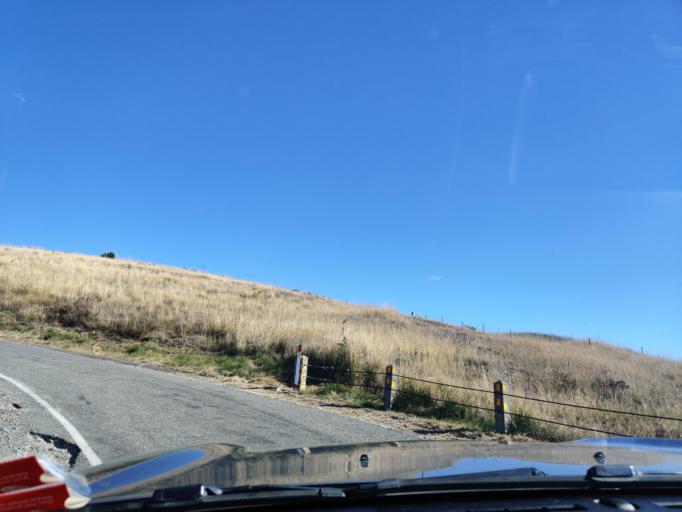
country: NZ
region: Canterbury
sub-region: Timaru District
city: Pleasant Point
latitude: -43.9828
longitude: 170.4654
